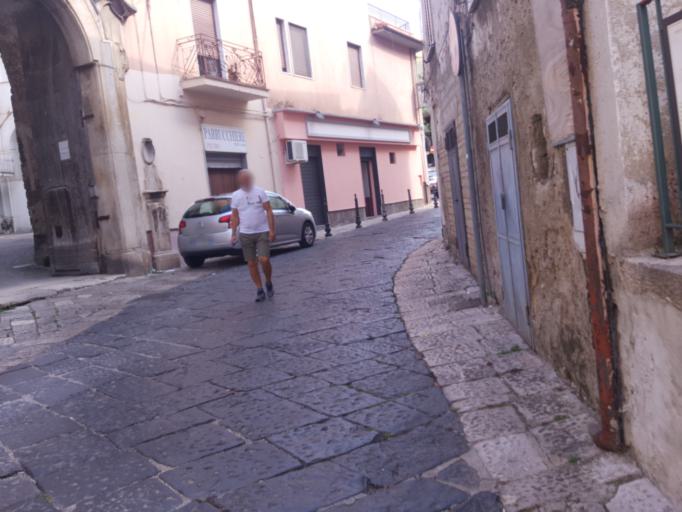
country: IT
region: Campania
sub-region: Provincia di Caserta
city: Pignataro Maggiore
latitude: 41.1911
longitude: 14.1719
